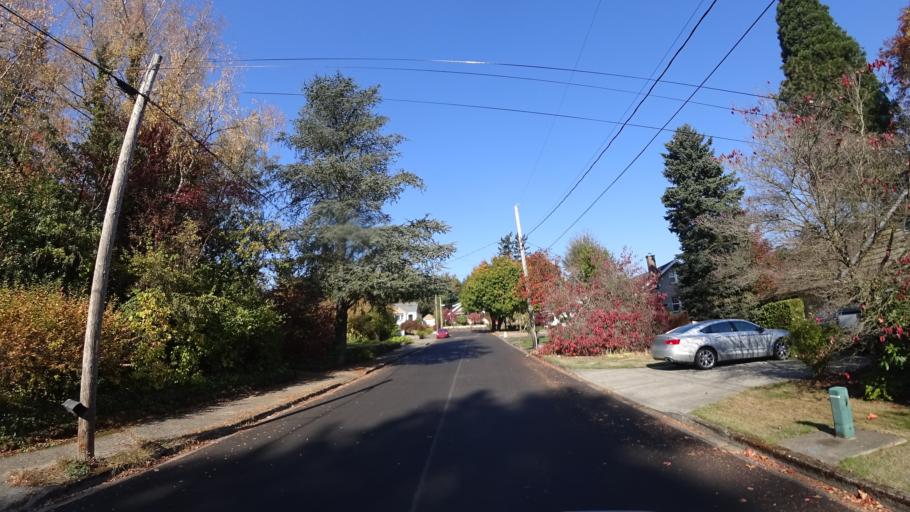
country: US
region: Oregon
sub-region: Multnomah County
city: Gresham
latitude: 45.4981
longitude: -122.4431
